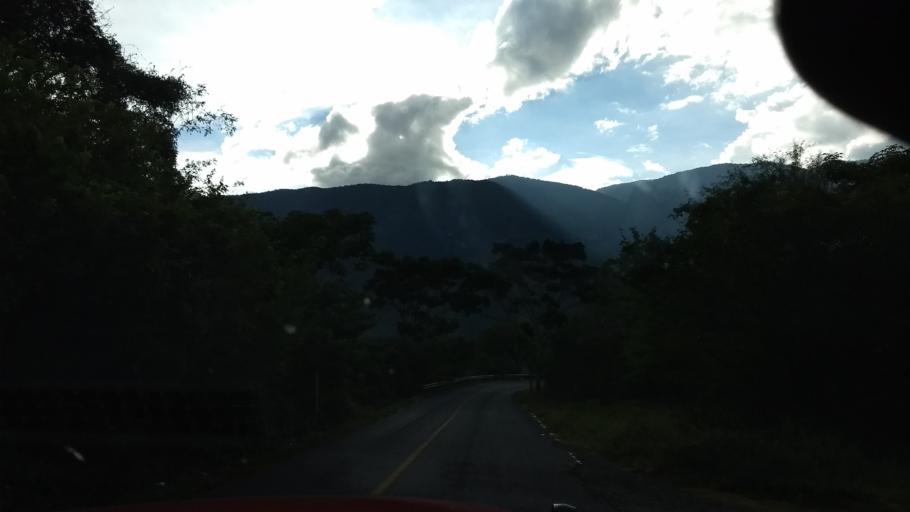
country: MX
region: Colima
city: Suchitlan
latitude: 19.4551
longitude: -103.8244
